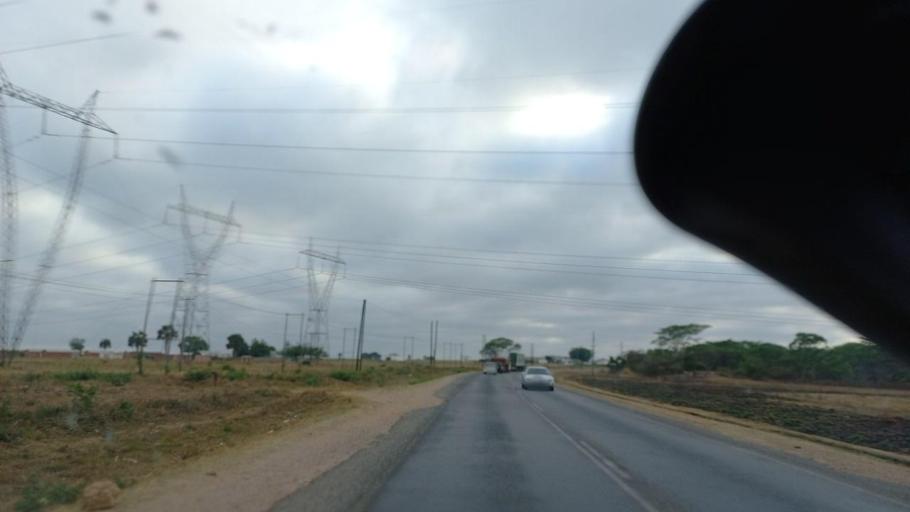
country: ZM
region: Lusaka
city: Chongwe
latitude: -15.3427
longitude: 28.5169
